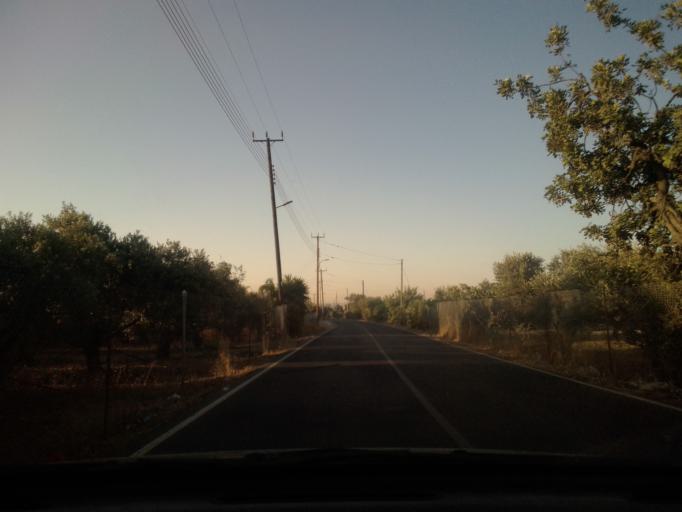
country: CY
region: Limassol
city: Ypsonas
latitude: 34.6760
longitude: 32.9576
